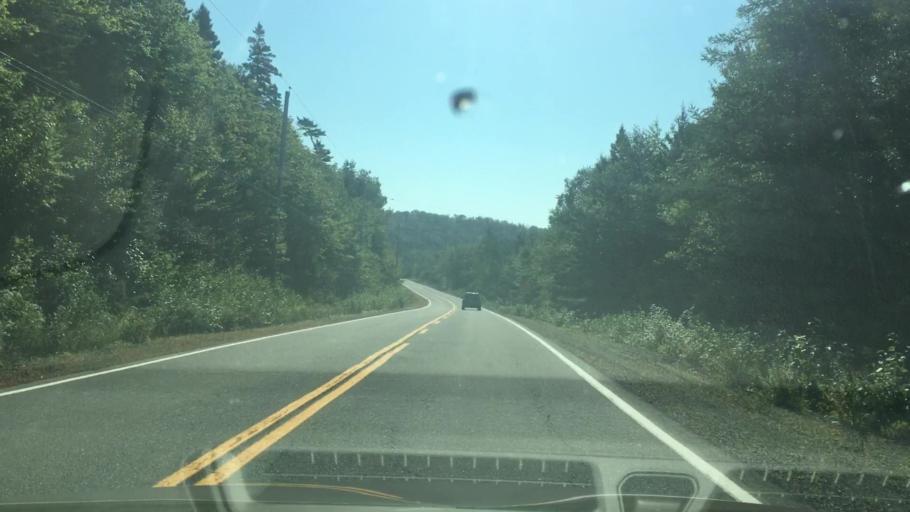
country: CA
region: Nova Scotia
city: Cole Harbour
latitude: 44.8074
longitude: -62.8329
